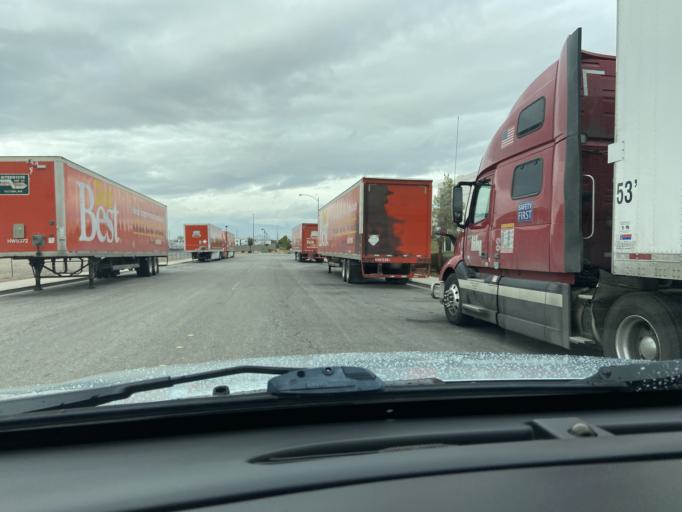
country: US
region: Nevada
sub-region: Clark County
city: North Las Vegas
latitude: 36.2434
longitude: -115.1065
